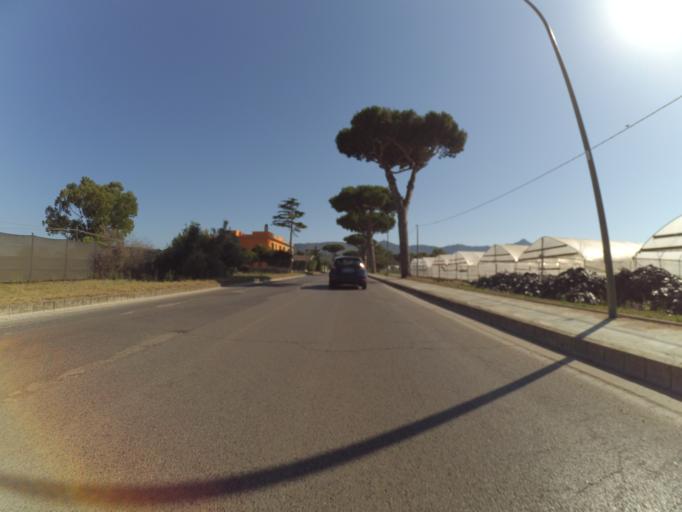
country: IT
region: Latium
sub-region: Provincia di Latina
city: San Felice Circeo
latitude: 41.2623
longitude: 13.0930
